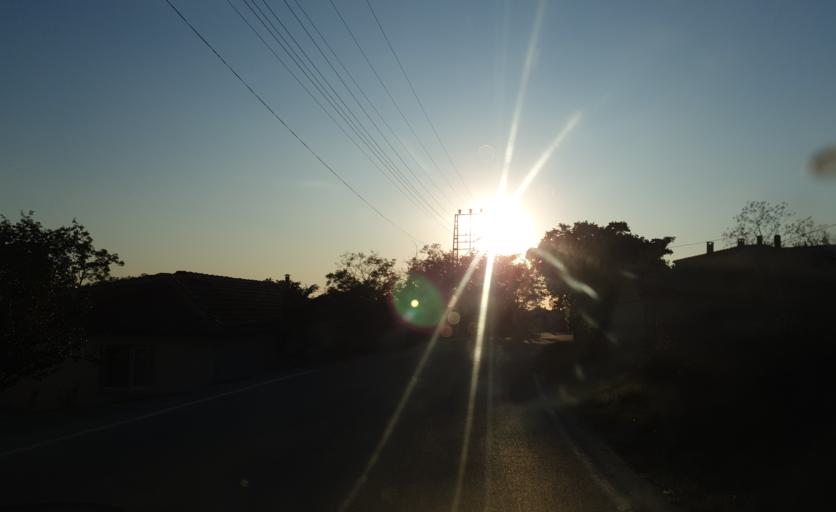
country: TR
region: Tekirdag
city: Beyazkoy
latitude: 41.3359
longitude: 27.7340
